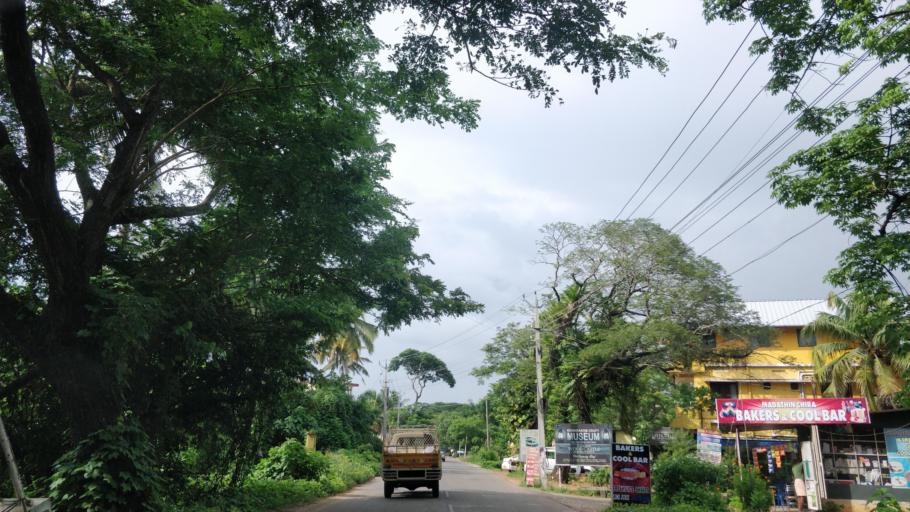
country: IN
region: Kerala
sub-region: Alappuzha
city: Shertallai
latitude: 9.6316
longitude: 76.4301
